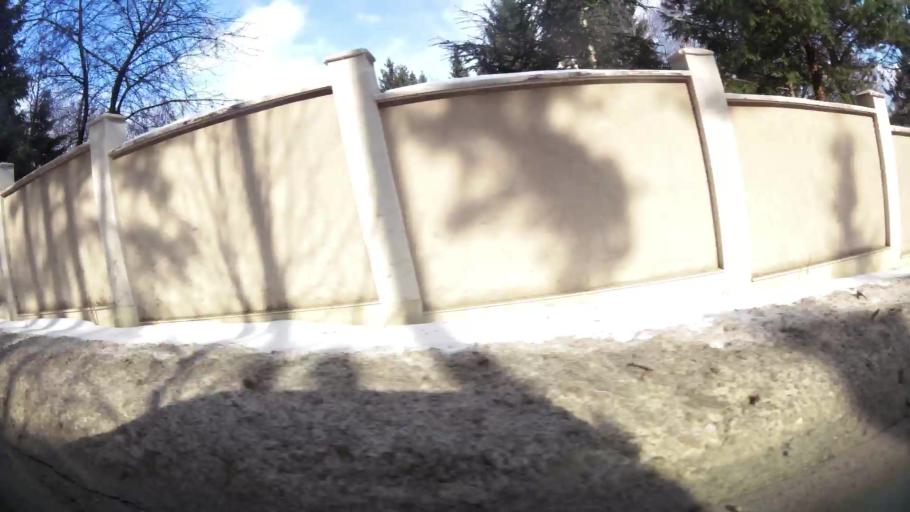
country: BG
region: Sofia-Capital
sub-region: Stolichna Obshtina
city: Sofia
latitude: 42.6460
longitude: 23.2436
